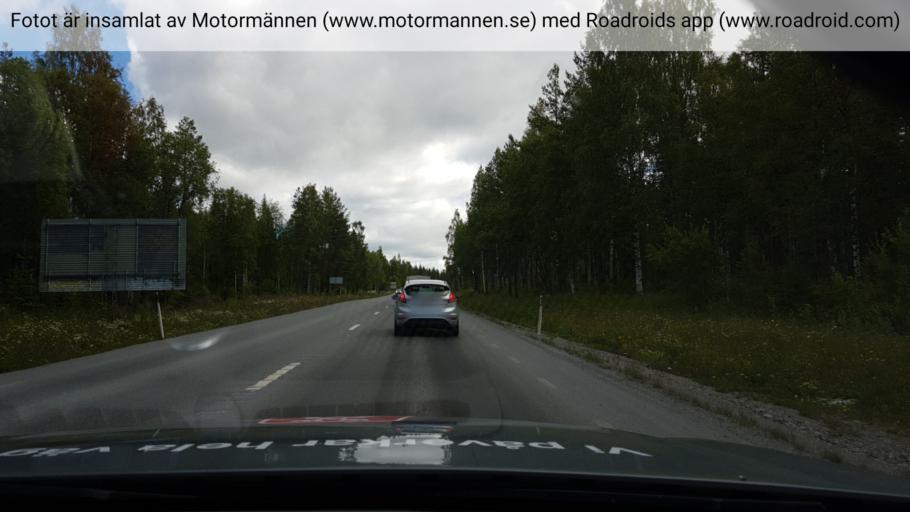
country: SE
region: Jaemtland
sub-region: OEstersunds Kommun
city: Ostersund
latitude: 63.1811
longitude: 14.6991
